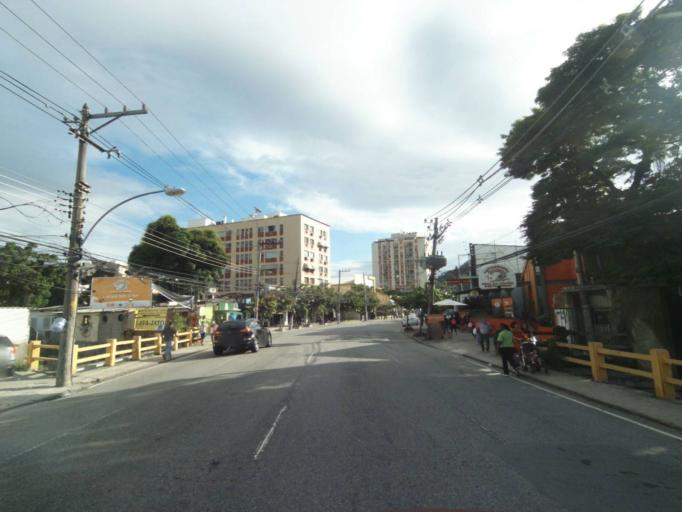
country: BR
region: Rio de Janeiro
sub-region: Rio De Janeiro
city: Rio de Janeiro
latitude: -22.9383
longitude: -43.3392
